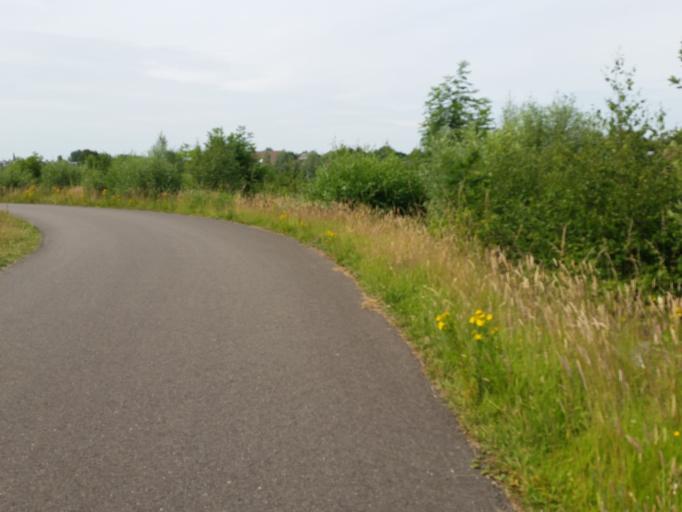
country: BE
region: Flanders
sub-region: Provincie Antwerpen
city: Boom
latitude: 51.0805
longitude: 4.3824
